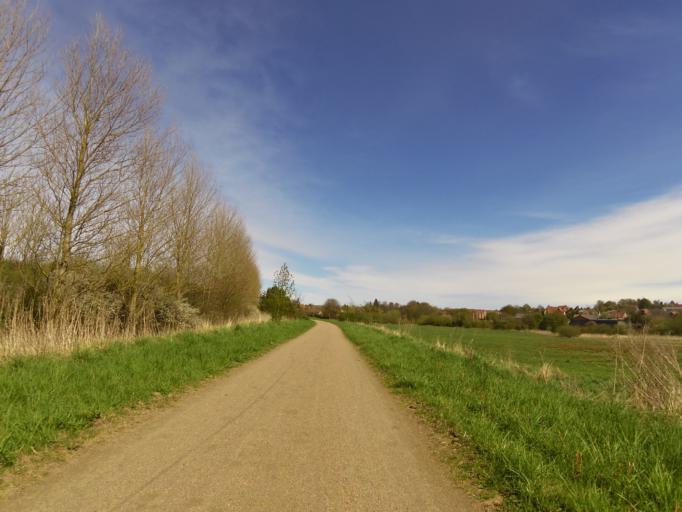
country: DK
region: Central Jutland
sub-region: Skive Kommune
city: Skive
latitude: 56.5764
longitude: 9.0192
